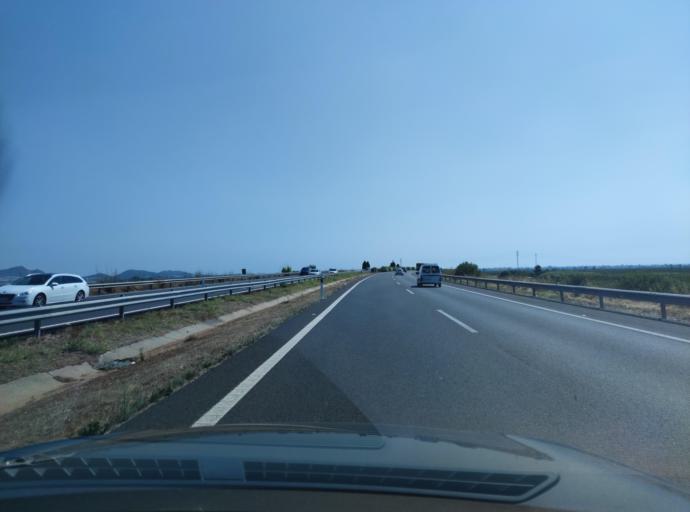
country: ES
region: Valencia
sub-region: Provincia de Valencia
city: Faura
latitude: 39.7032
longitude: -0.2560
